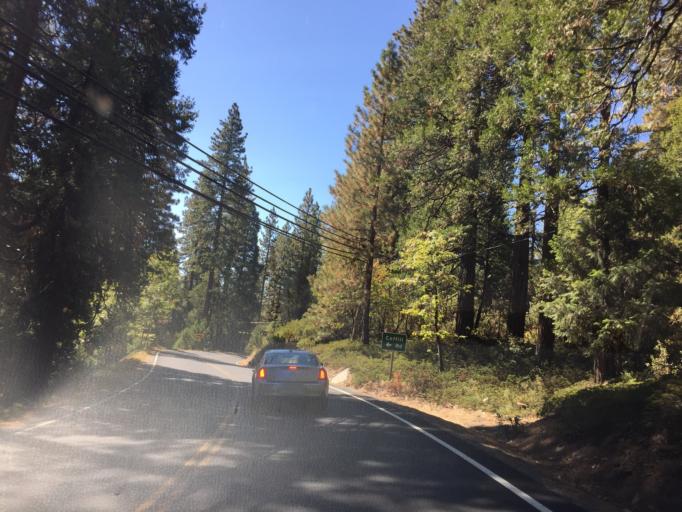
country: US
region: California
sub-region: Tuolumne County
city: Twain Harte
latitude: 38.0481
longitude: -120.2038
